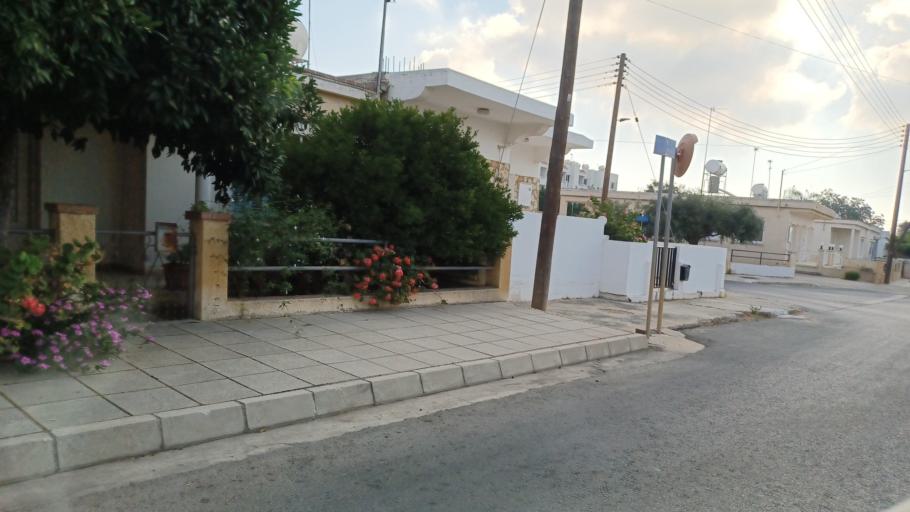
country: CY
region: Ammochostos
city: Deryneia
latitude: 35.0632
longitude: 33.9635
